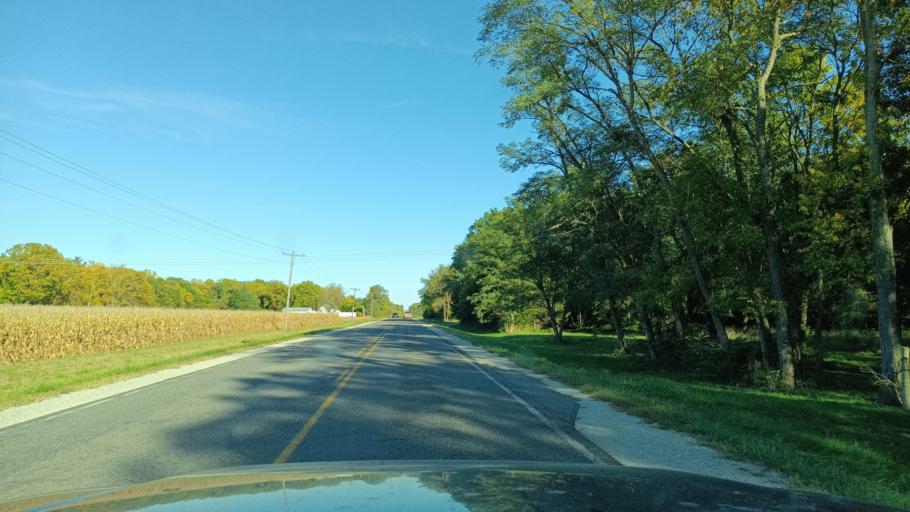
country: US
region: Illinois
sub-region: McLean County
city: Le Roy
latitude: 40.2245
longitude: -88.8298
